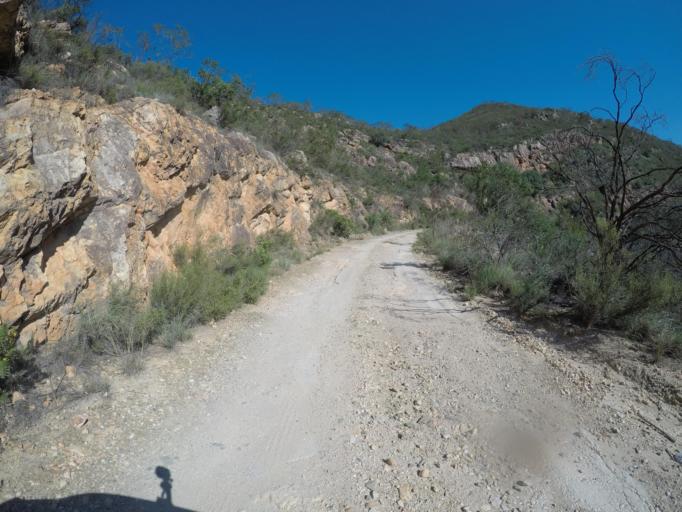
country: ZA
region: Eastern Cape
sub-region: Cacadu District Municipality
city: Kareedouw
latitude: -33.6537
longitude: 24.5065
